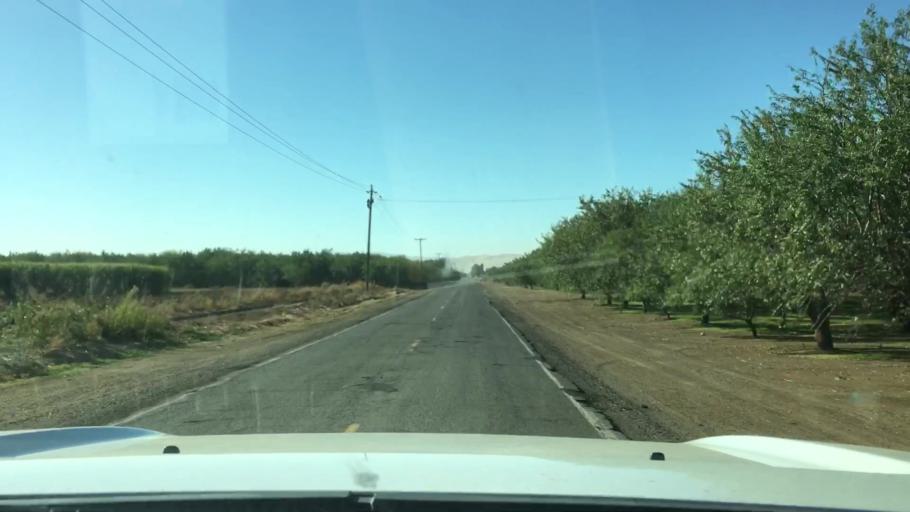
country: US
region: California
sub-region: Merced County
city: Gustine
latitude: 37.1523
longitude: -121.0321
